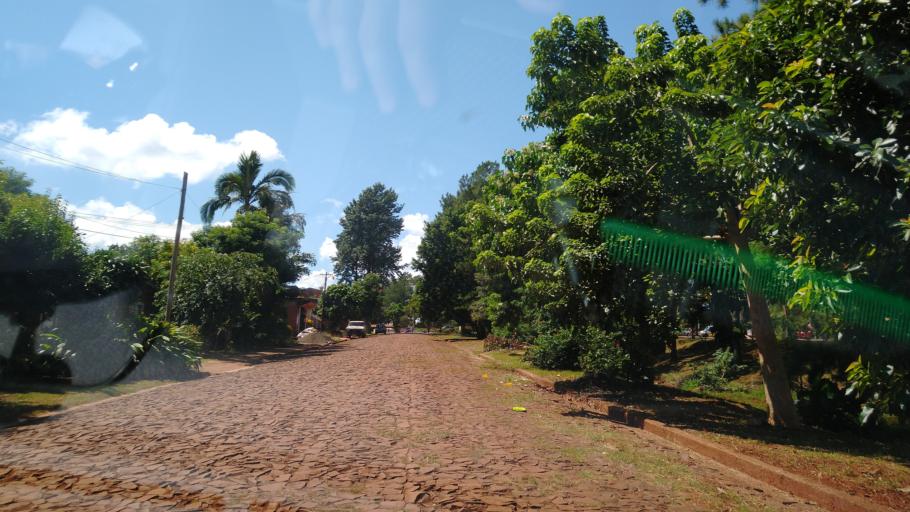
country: AR
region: Misiones
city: Puerto Libertad
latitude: -25.9695
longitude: -54.5621
